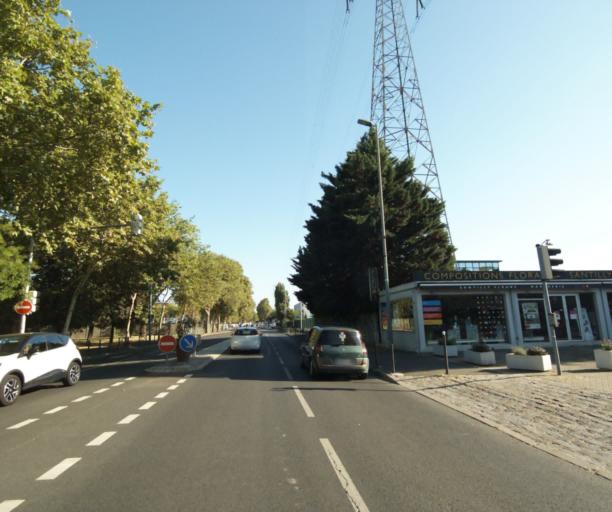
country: FR
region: Ile-de-France
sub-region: Departement des Hauts-de-Seine
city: Villeneuve-la-Garenne
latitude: 48.9366
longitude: 2.3245
